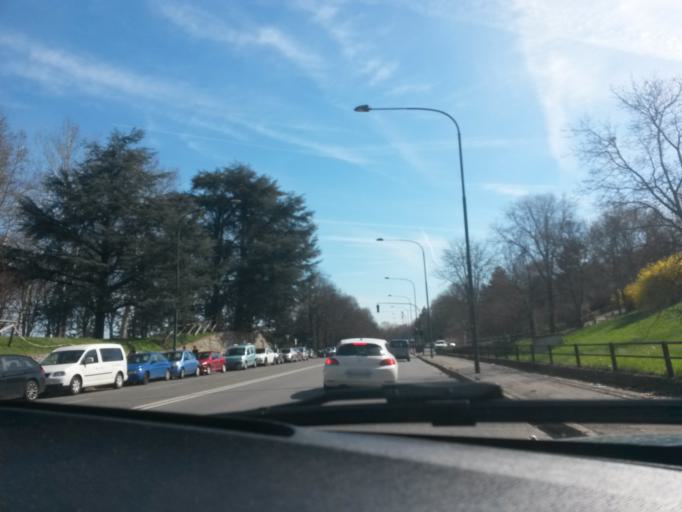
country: IT
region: Piedmont
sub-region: Provincia di Torino
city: Lesna
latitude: 45.0847
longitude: 7.6422
